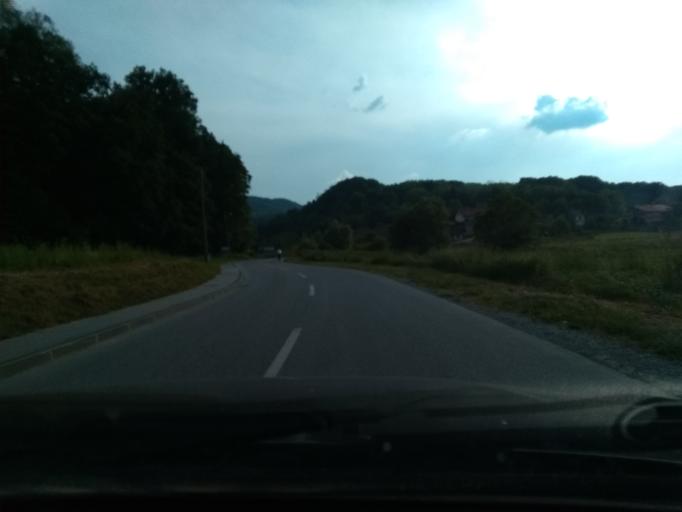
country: SI
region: Bistrica ob Sotli
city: Bistrica ob Sotli
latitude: 46.0744
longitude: 15.7453
